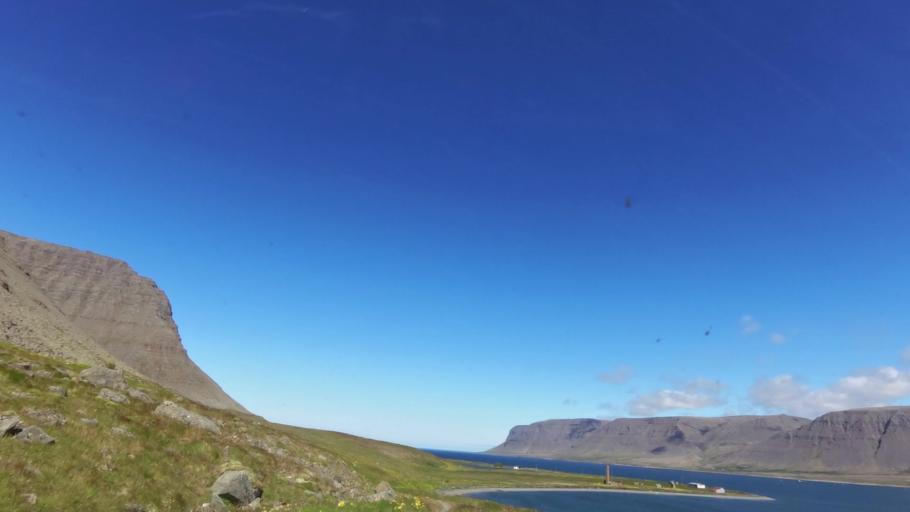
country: IS
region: West
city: Olafsvik
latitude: 65.6353
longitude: -23.9266
